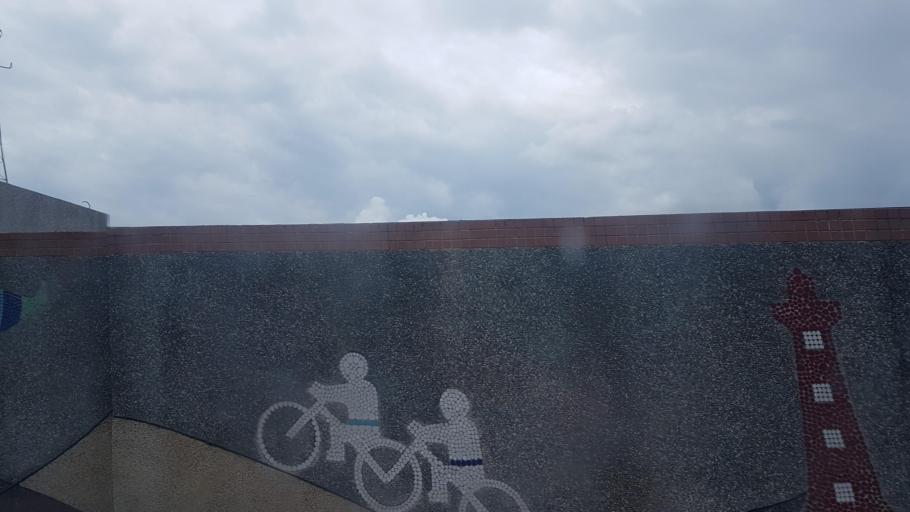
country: TW
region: Taiwan
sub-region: Hualien
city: Hualian
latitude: 24.0058
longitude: 121.6387
